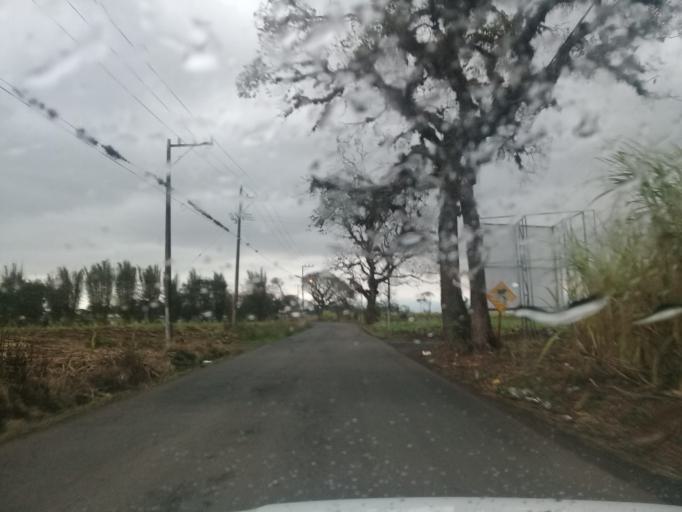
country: MX
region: Veracruz
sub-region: Cordoba
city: San Jose de Tapia
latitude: 18.8516
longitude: -96.9505
